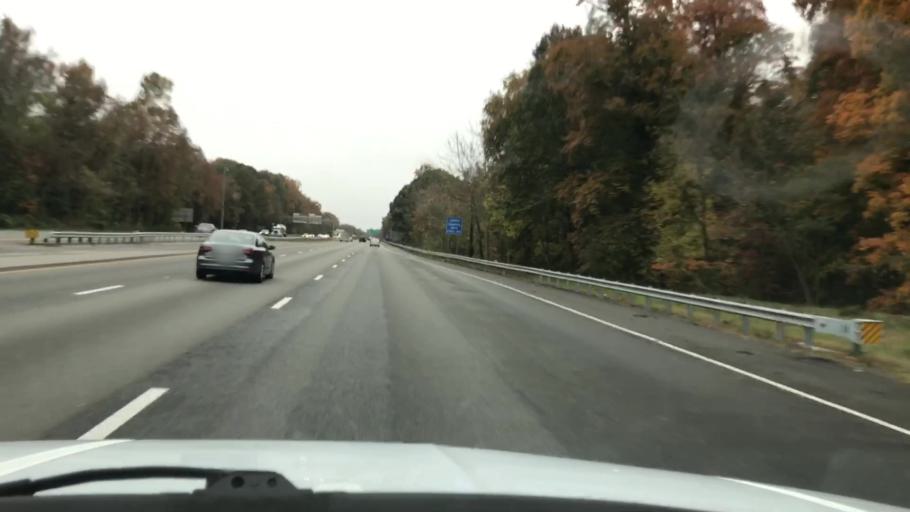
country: US
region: Virginia
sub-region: Henrico County
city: Chamberlayne
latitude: 37.6236
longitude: -77.4455
